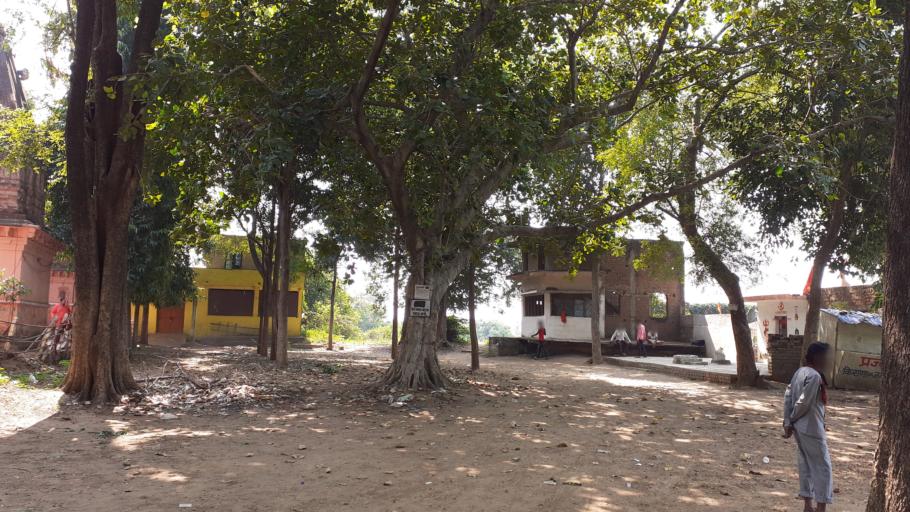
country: IN
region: Maharashtra
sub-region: Nagpur Division
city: Kamthi
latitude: 21.2698
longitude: 79.1680
